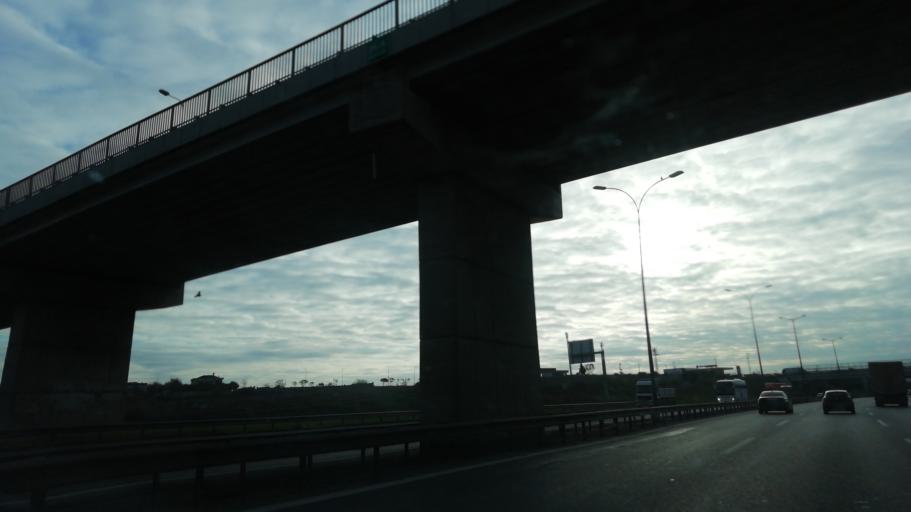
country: TR
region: Istanbul
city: Sultanbeyli
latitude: 40.9287
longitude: 29.3475
